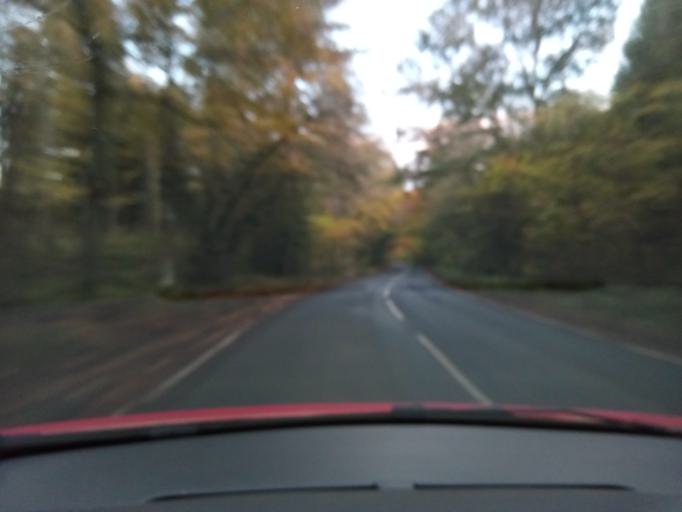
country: GB
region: England
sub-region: Northumberland
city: Bardon Mill
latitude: 54.9530
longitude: -2.2651
